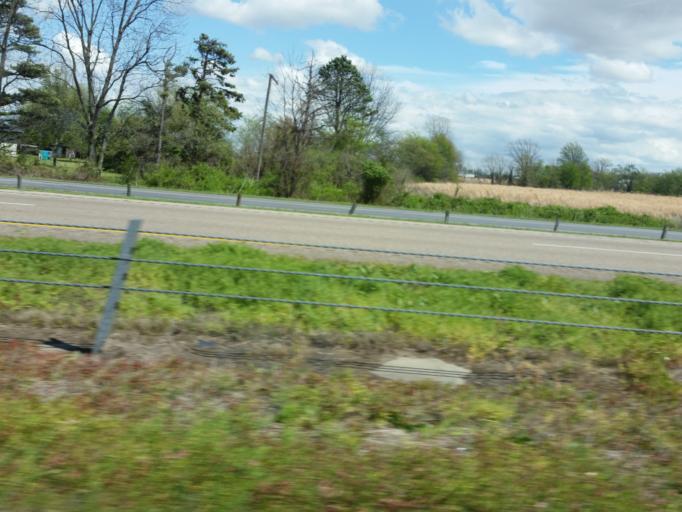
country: US
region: Arkansas
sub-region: Crittenden County
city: Marion
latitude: 35.2255
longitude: -90.2115
